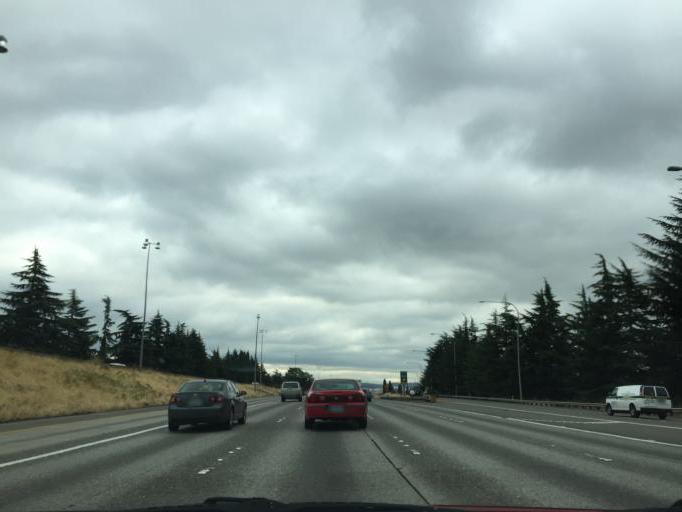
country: US
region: Washington
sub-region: King County
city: Seattle
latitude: 47.5568
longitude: -122.3205
